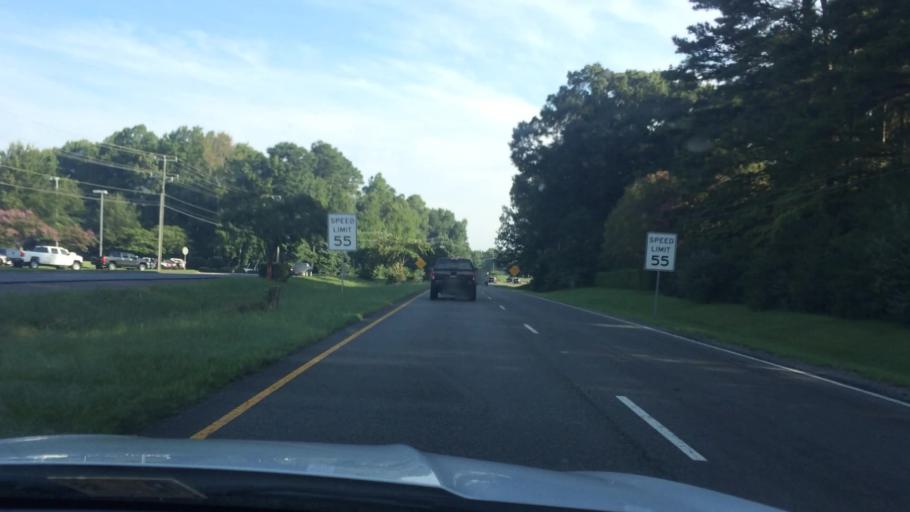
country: US
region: Virginia
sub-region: Gloucester County
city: Gloucester Courthouse
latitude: 37.3761
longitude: -76.5349
